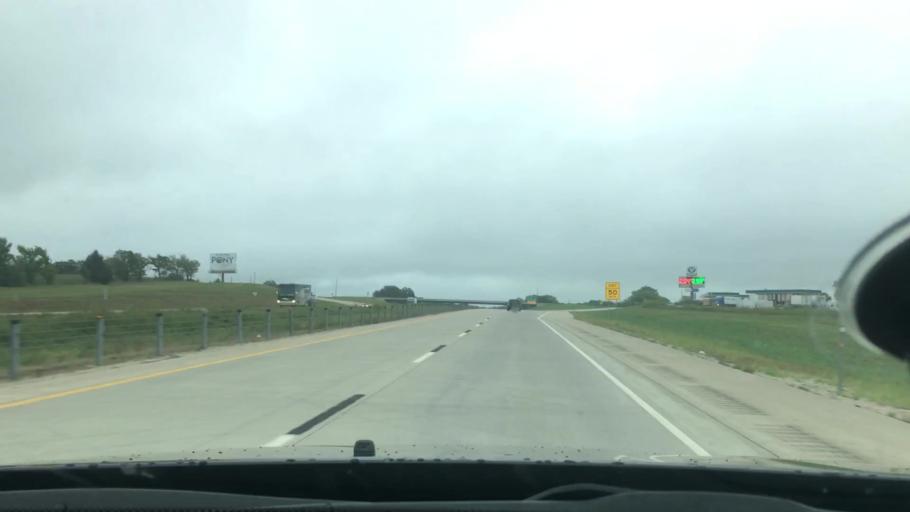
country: US
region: Oklahoma
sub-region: Okfuskee County
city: Boley
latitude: 35.3852
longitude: -96.4649
